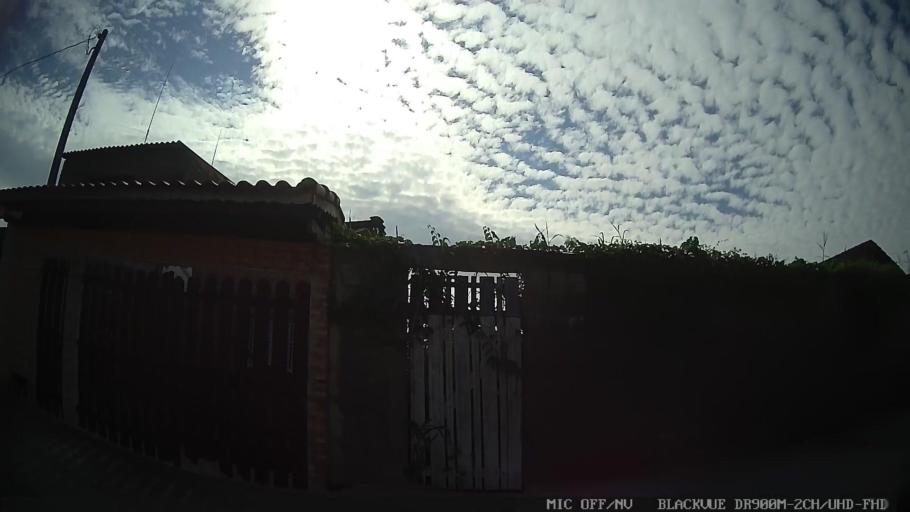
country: BR
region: Sao Paulo
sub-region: Itanhaem
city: Itanhaem
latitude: -24.1582
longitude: -46.7516
